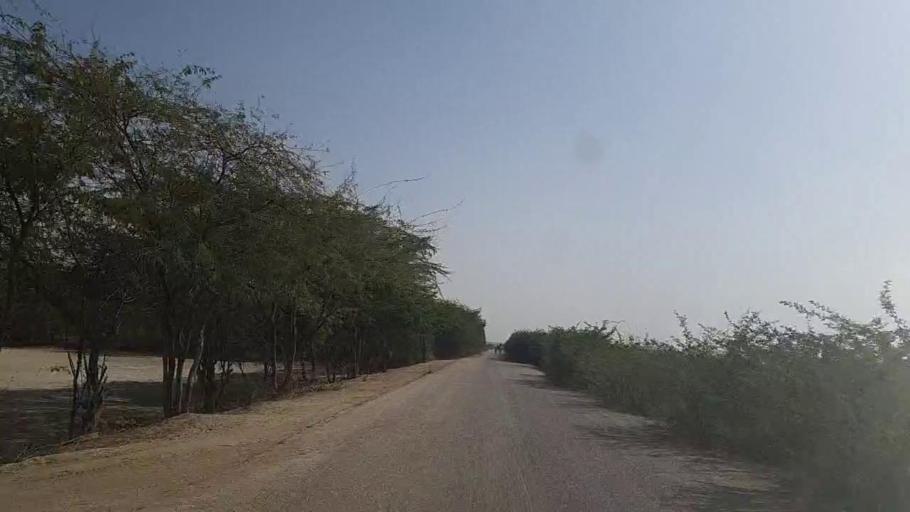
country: PK
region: Sindh
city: Kadhan
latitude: 24.5616
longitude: 69.2764
